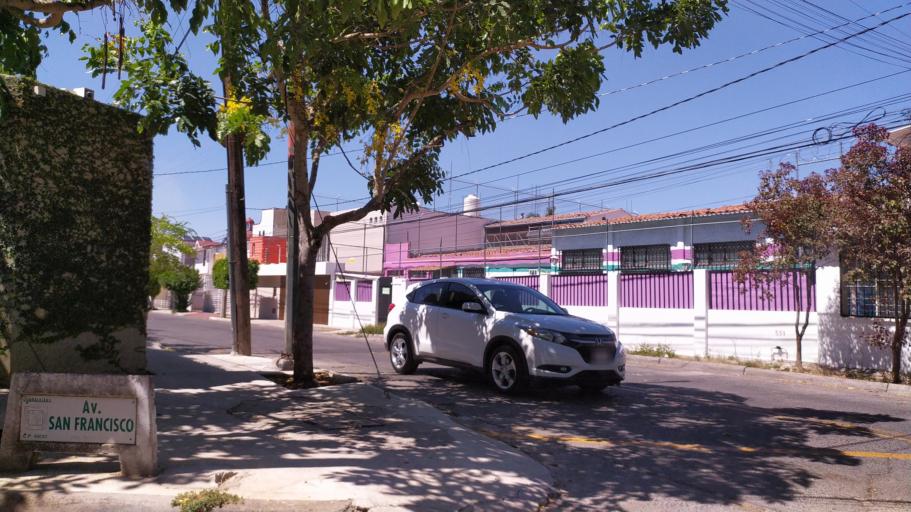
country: MX
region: Jalisco
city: Guadalajara
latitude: 20.6694
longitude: -103.3976
